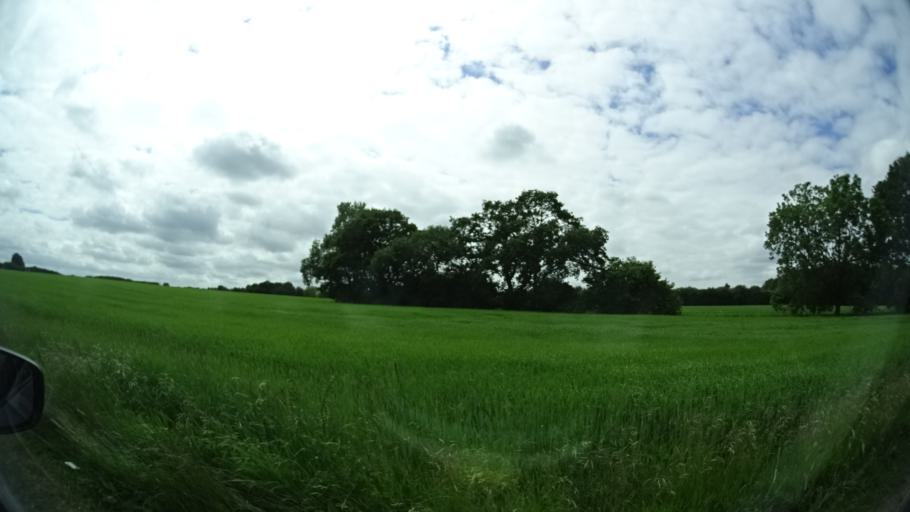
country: DK
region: Central Jutland
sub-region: Syddjurs Kommune
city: Ryomgard
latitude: 56.4017
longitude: 10.5622
